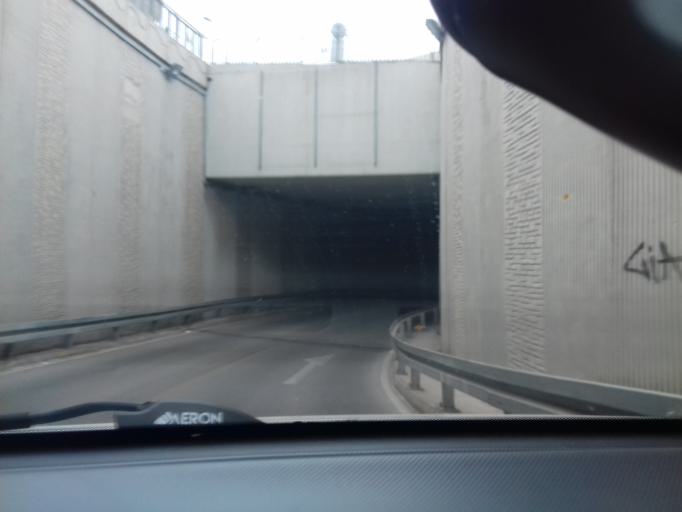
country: TR
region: Istanbul
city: Pendik
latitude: 40.8807
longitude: 29.2346
